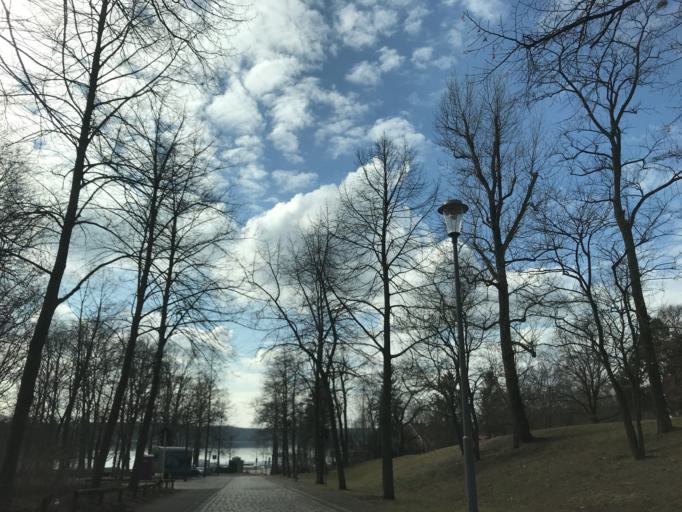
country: DE
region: Berlin
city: Kladow
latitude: 52.4541
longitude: 13.1491
